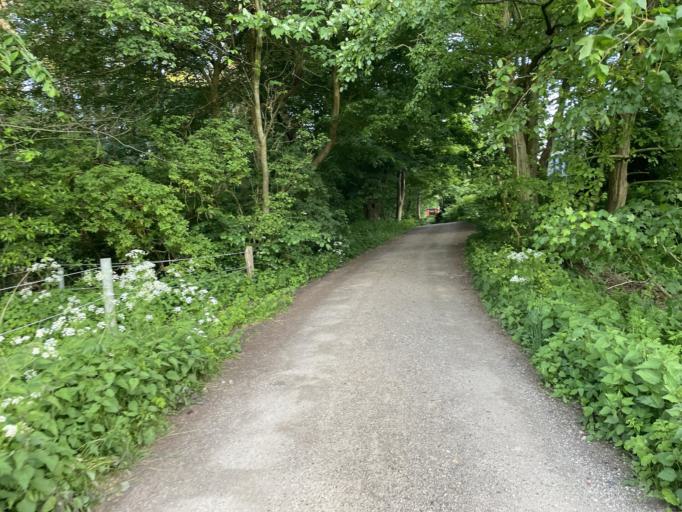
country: DE
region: Schleswig-Holstein
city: Husum
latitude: 54.4715
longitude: 9.0718
